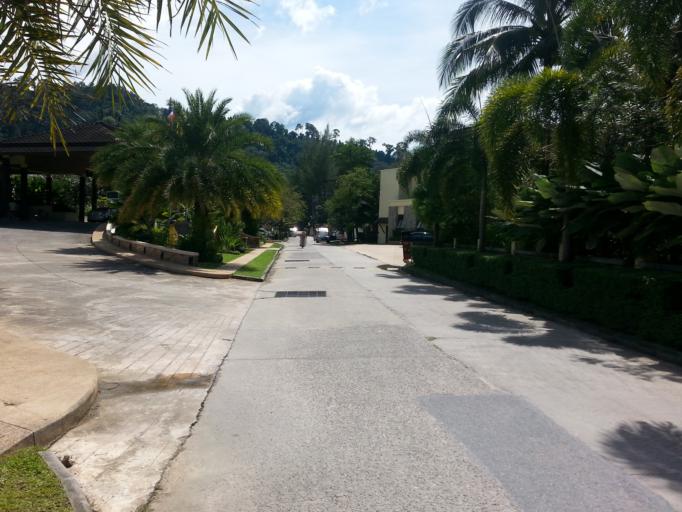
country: TH
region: Phangnga
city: Ban Khao Lak
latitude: 8.6431
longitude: 98.2475
